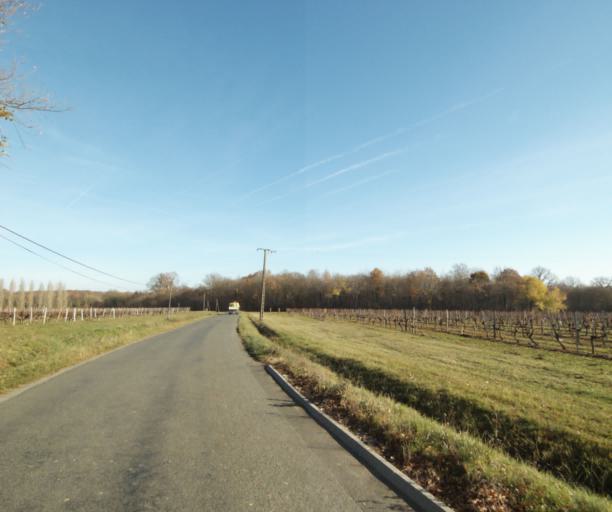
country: FR
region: Poitou-Charentes
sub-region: Departement de la Charente-Maritime
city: Cherac
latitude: 45.7261
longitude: -0.4550
